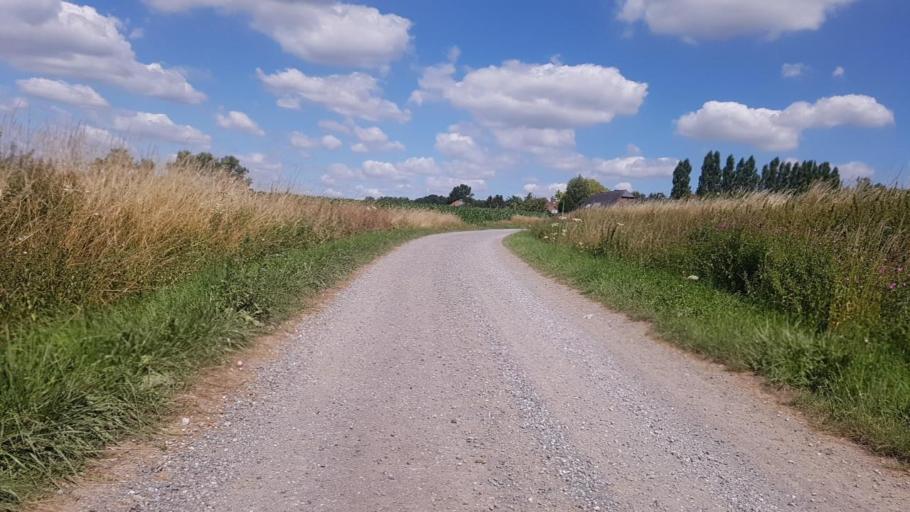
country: BE
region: Wallonia
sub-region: Province du Hainaut
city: Thuin
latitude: 50.3215
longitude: 4.3637
